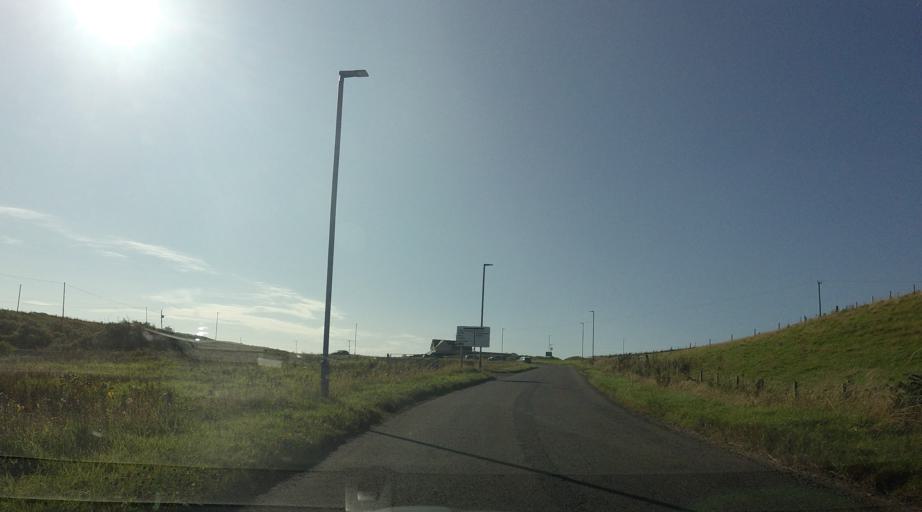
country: GB
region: Scotland
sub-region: Highland
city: Wick
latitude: 58.6370
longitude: -3.1608
